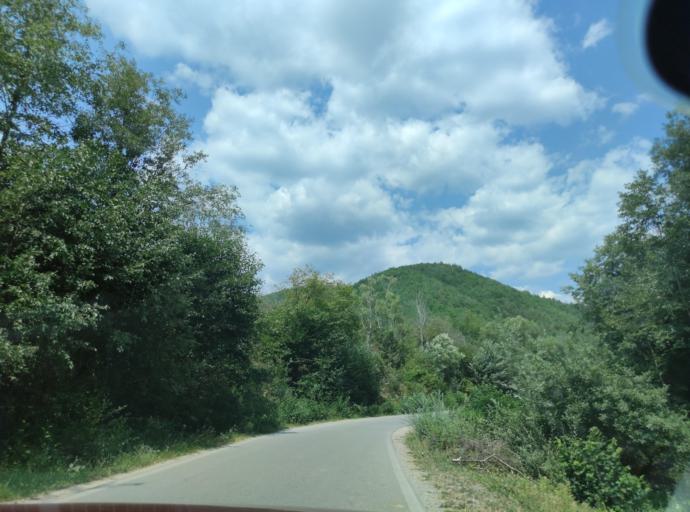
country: BG
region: Blagoevgrad
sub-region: Obshtina Belitsa
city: Belitsa
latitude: 42.0006
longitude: 23.5498
